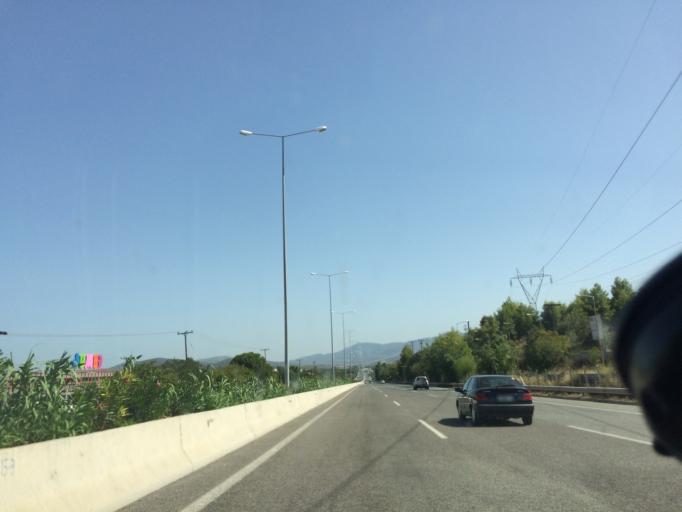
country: GR
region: Central Greece
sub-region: Nomos Voiotias
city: Oinofyta
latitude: 38.3059
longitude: 23.6487
